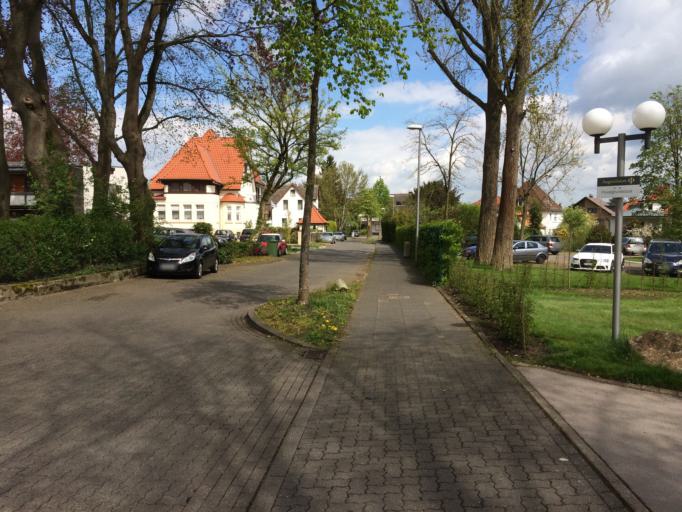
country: DE
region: North Rhine-Westphalia
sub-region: Regierungsbezirk Detmold
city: Detmold
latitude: 51.9219
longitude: 8.8449
